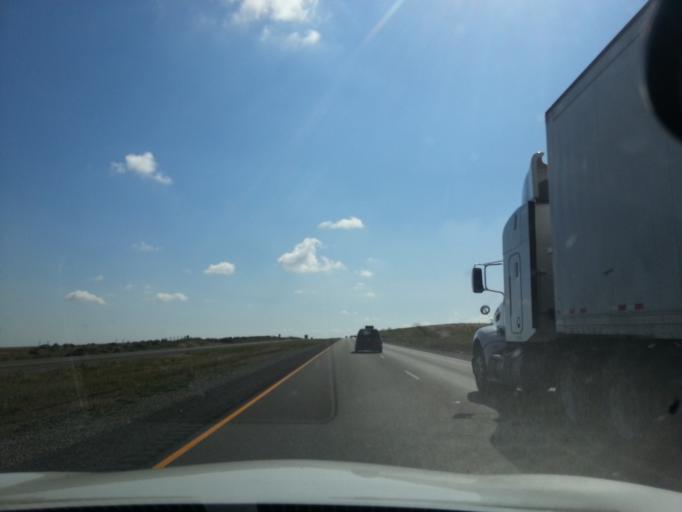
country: US
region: California
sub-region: Fresno County
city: Mendota
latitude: 36.5382
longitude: -120.4980
